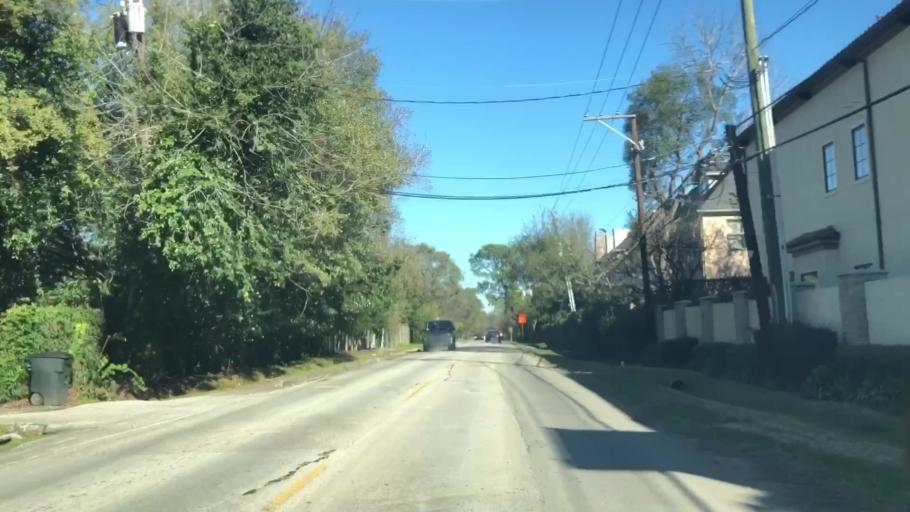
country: US
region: Texas
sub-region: Harris County
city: Hunters Creek Village
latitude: 29.7557
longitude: -95.4675
